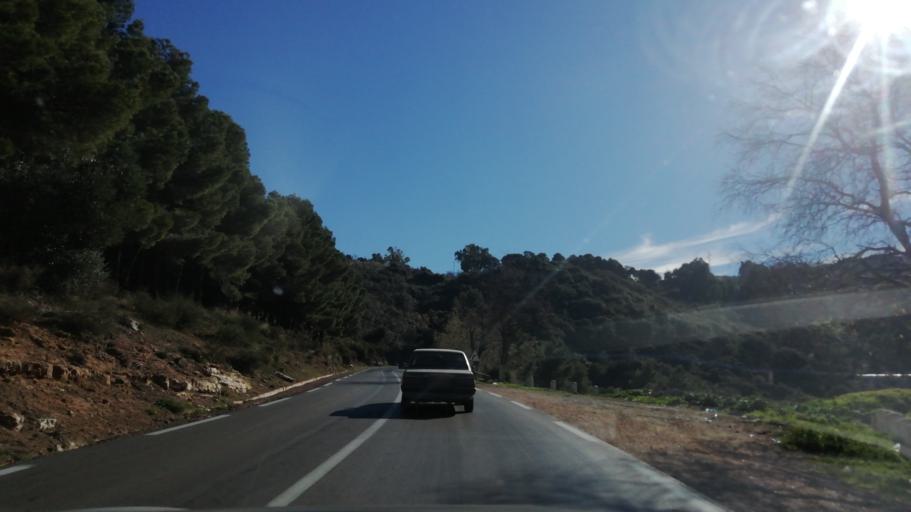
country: DZ
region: Tlemcen
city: Mansoura
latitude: 34.8522
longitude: -1.3524
